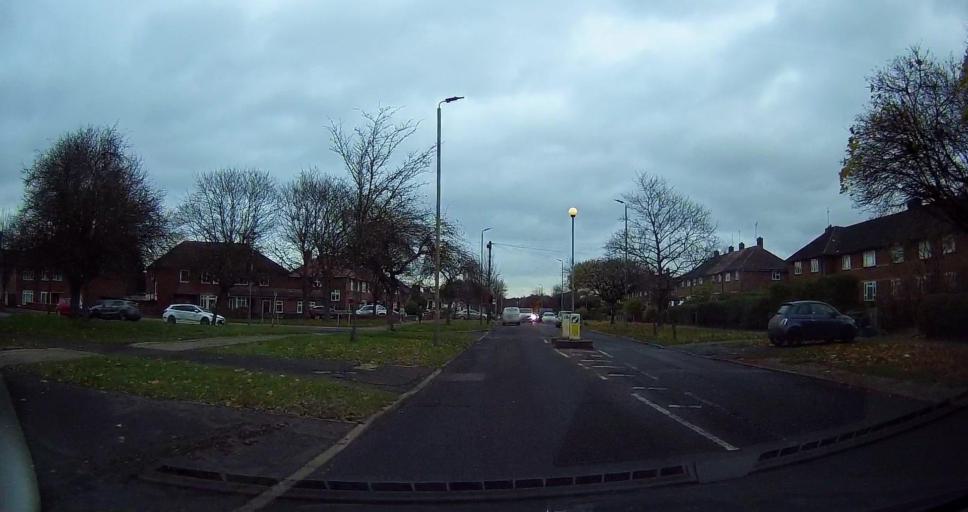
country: GB
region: England
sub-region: Greater London
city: Sidcup
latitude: 51.4089
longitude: 0.1063
